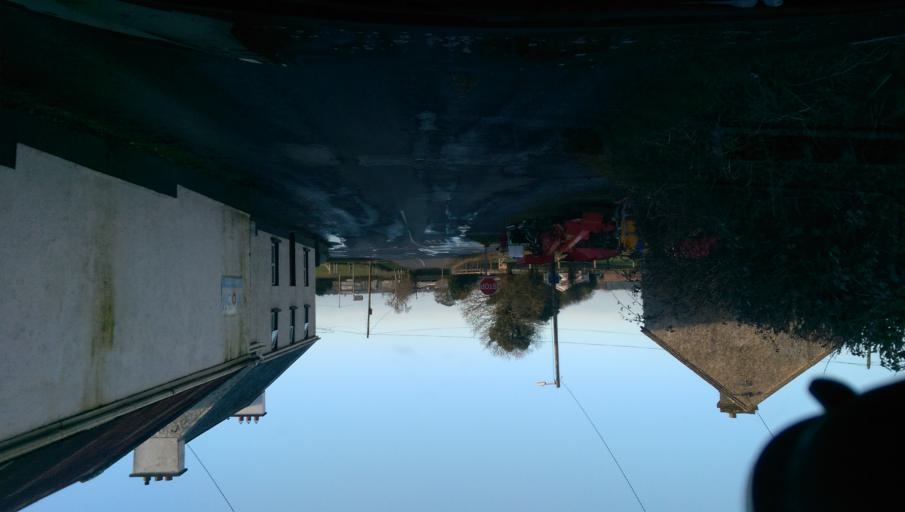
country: IE
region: Connaught
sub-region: County Galway
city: Loughrea
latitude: 53.3934
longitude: -8.4812
